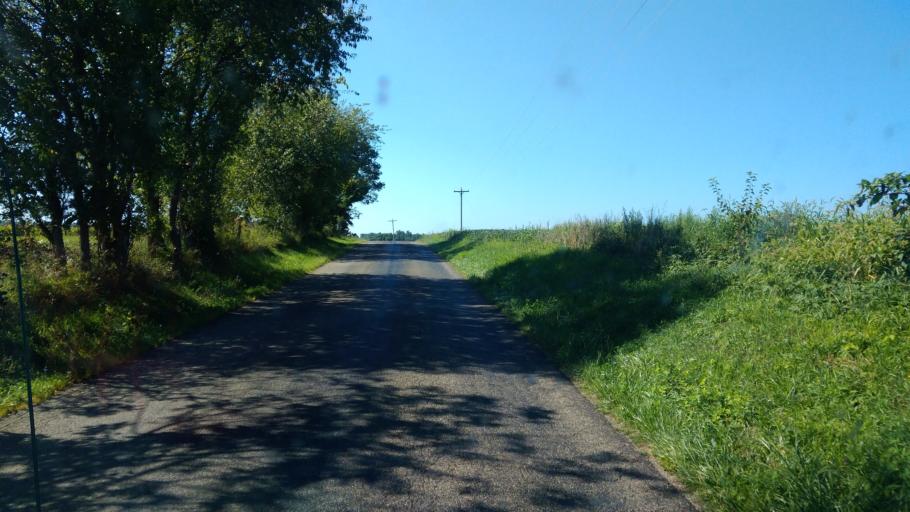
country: US
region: Ohio
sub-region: Knox County
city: Mount Vernon
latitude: 40.4597
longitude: -82.4674
